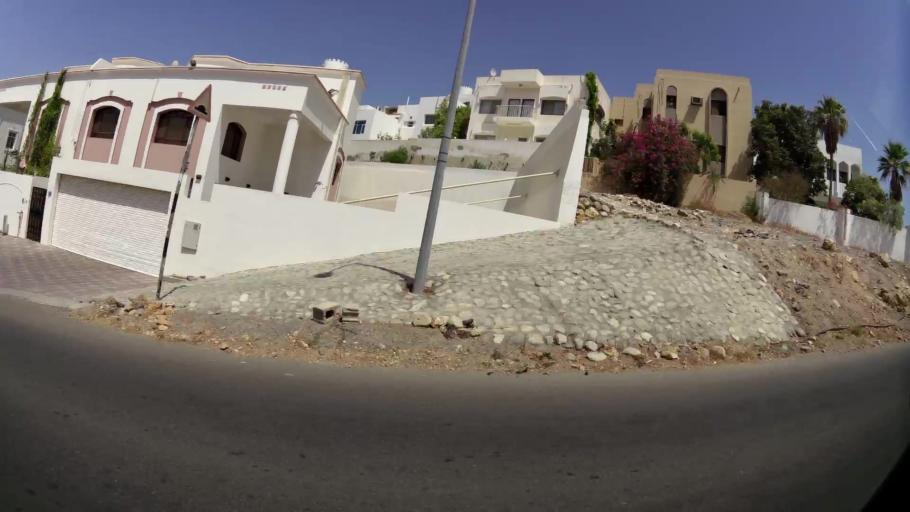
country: OM
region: Muhafazat Masqat
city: Muscat
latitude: 23.6180
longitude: 58.5037
